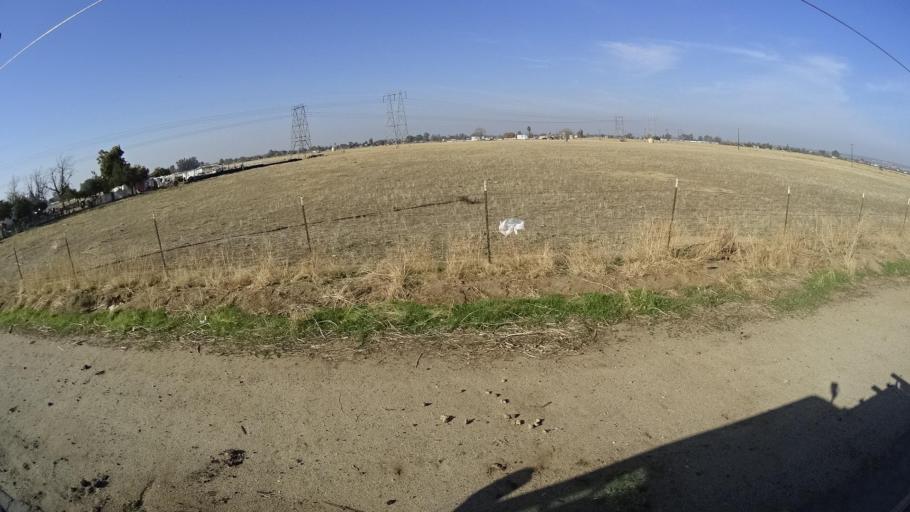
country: US
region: California
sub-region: Kern County
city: Lamont
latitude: 35.3385
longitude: -118.8964
